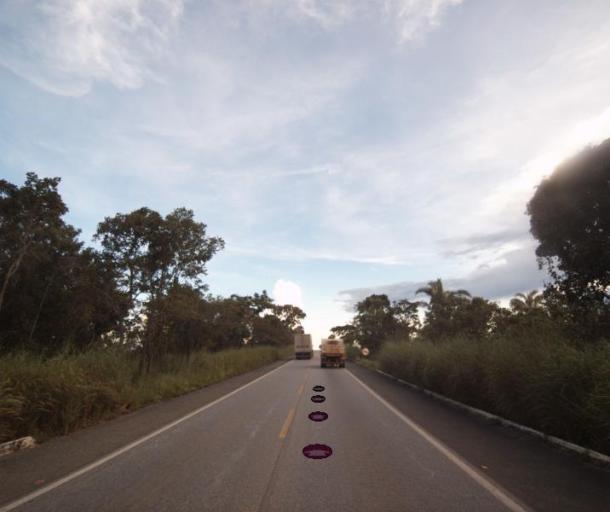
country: BR
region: Goias
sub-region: Uruacu
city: Uruacu
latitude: -14.2453
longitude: -49.1381
